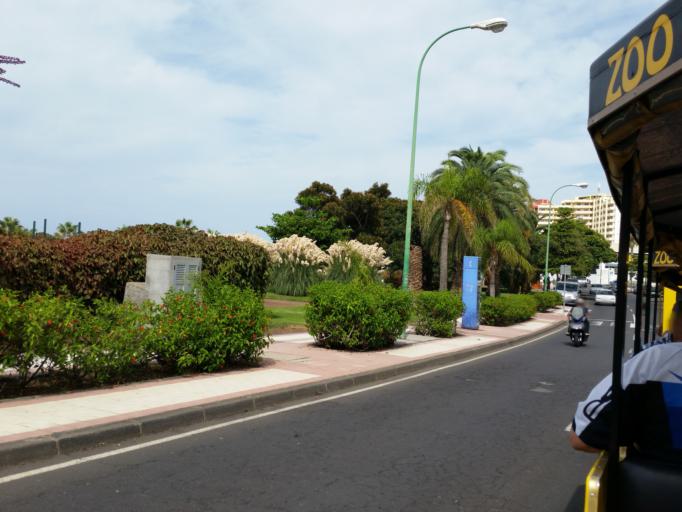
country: ES
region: Canary Islands
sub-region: Provincia de Santa Cruz de Tenerife
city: Puerto de la Cruz
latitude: 28.4116
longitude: -16.5599
